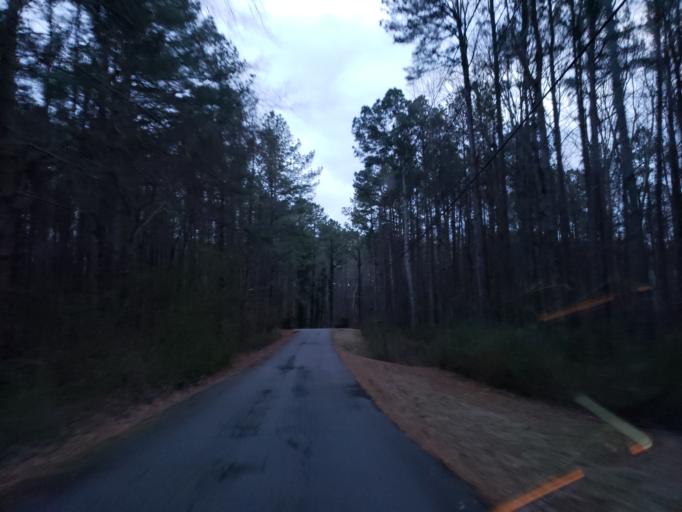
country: US
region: Georgia
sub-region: Cobb County
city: Kennesaw
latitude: 34.0288
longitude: -84.6329
